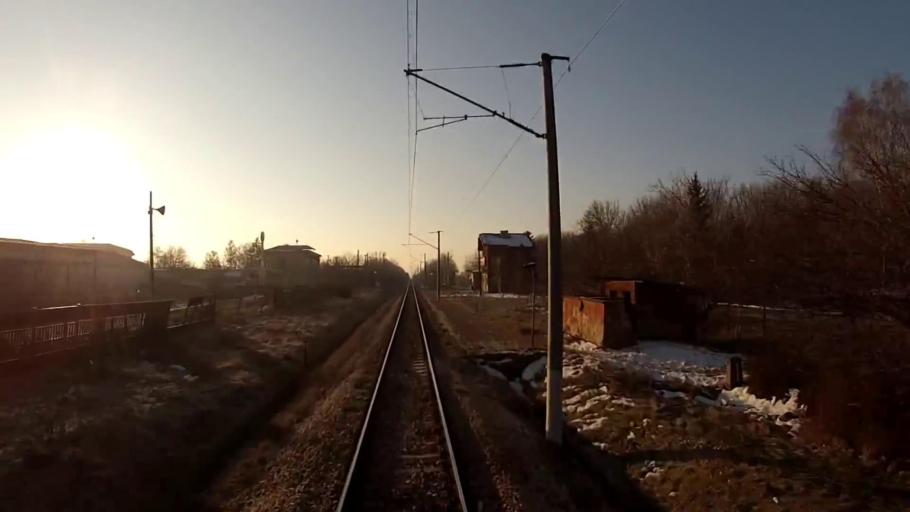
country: BG
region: Sofiya
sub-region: Obshtina Kostinbrod
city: Kostinbrod
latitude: 42.7898
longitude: 23.2113
